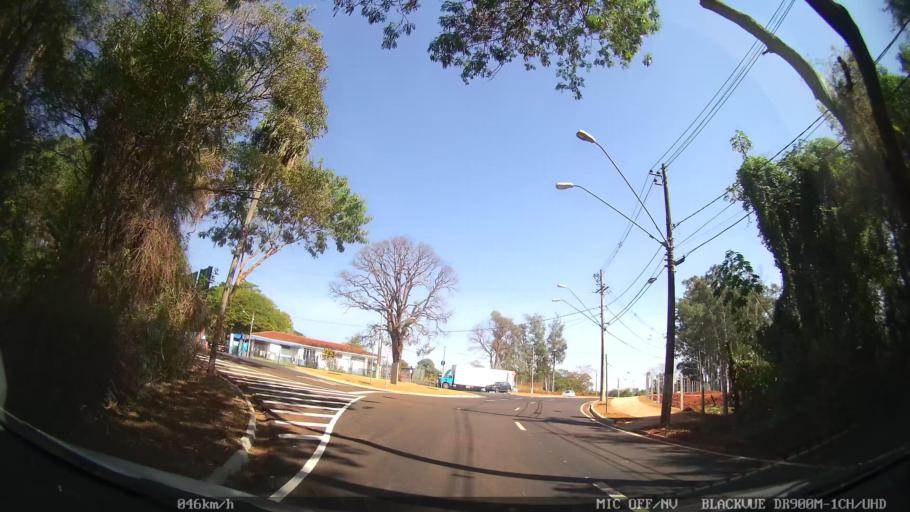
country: BR
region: Sao Paulo
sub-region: Ribeirao Preto
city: Ribeirao Preto
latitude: -21.2054
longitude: -47.8283
